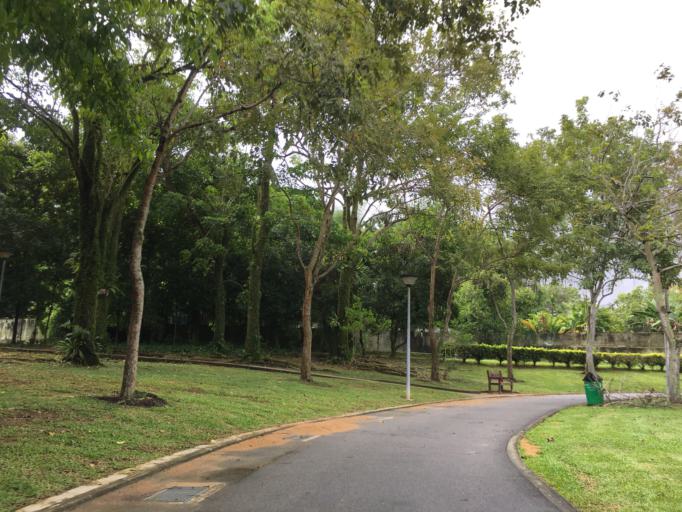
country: SG
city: Singapore
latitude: 1.3756
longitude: 103.8992
